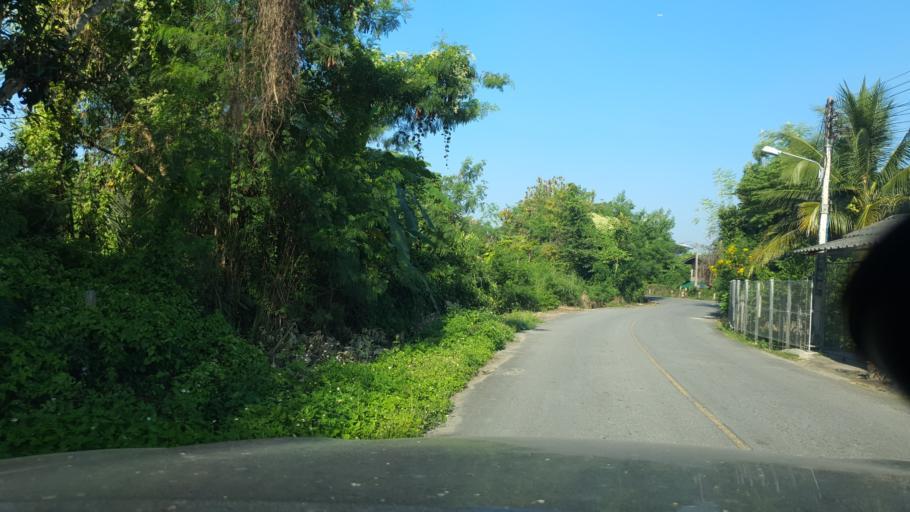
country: TH
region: Chiang Mai
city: San Kamphaeng
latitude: 18.7523
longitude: 99.1428
